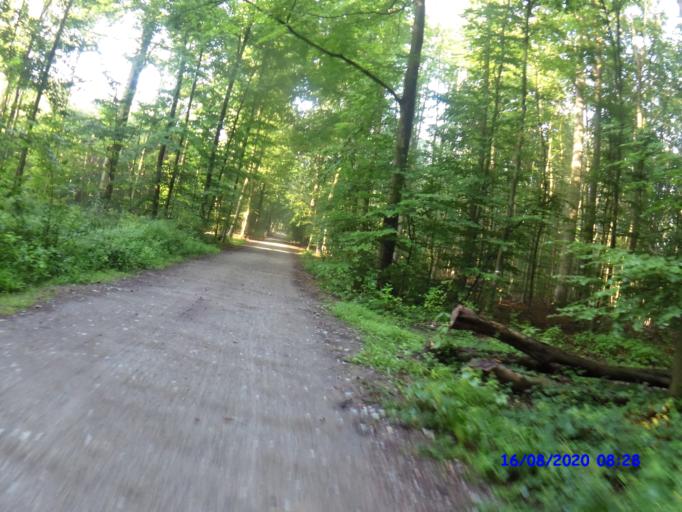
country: BE
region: Flanders
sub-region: Provincie Vlaams-Brabant
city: Sint-Genesius-Rode
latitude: 50.7829
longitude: 4.3977
